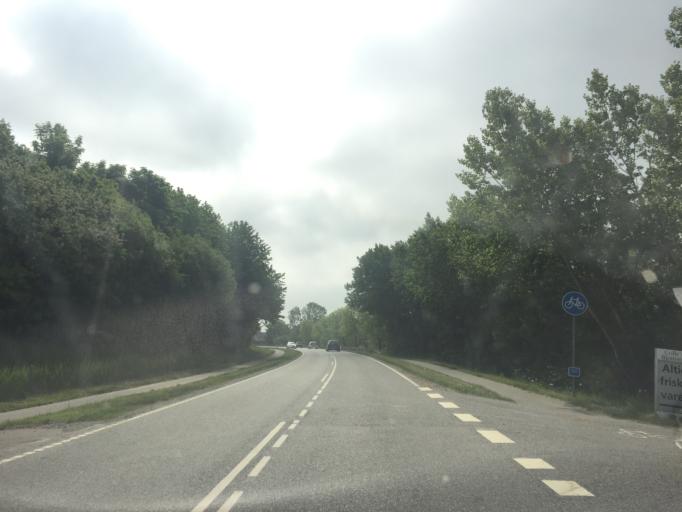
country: DK
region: South Denmark
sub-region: Kolding Kommune
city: Sonder Bjert
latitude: 55.4630
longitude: 9.5357
